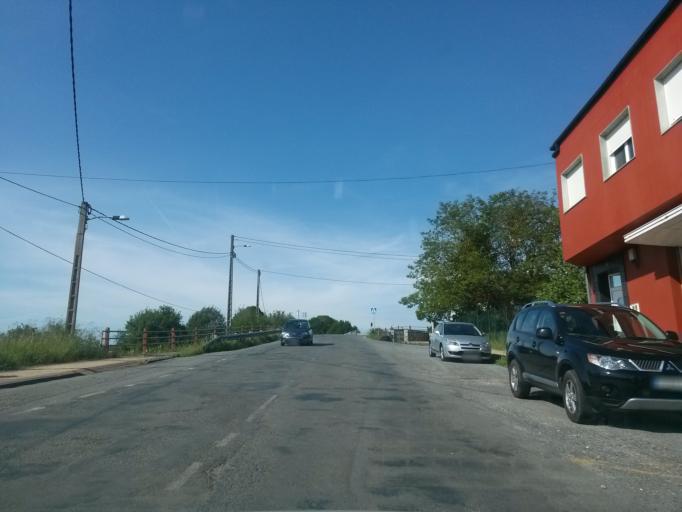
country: ES
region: Galicia
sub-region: Provincia de Lugo
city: Lugo
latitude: 43.0323
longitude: -7.5589
